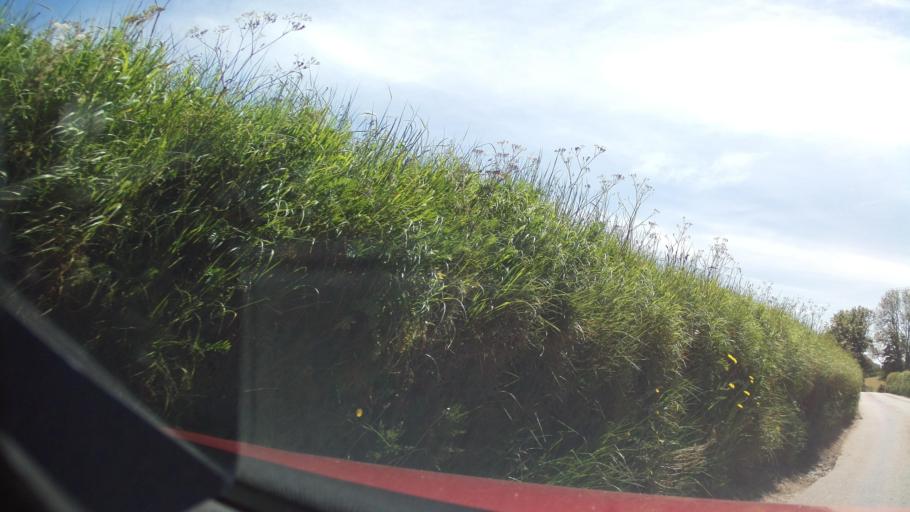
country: GB
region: England
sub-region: Devon
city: Ottery St Mary
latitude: 50.7456
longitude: -3.2761
